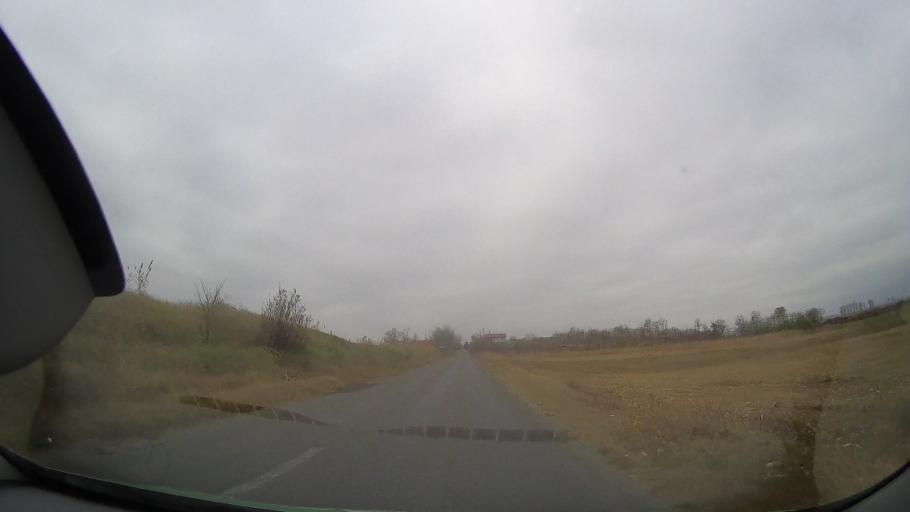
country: RO
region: Buzau
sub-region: Comuna Luciu
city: Luciu
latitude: 44.9797
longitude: 27.0449
